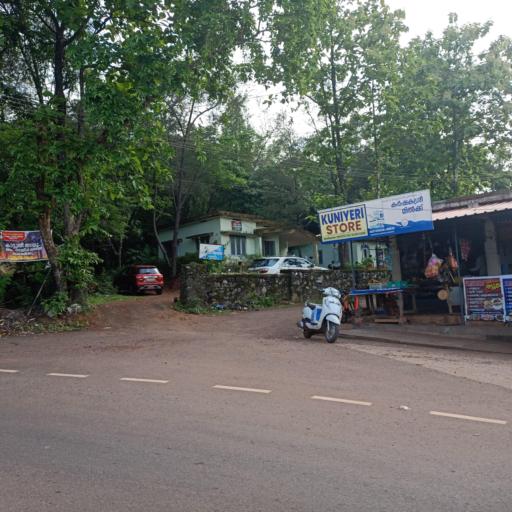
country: IN
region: Kerala
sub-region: Kasaragod District
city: Kasaragod
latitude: 12.5048
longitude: 75.0972
